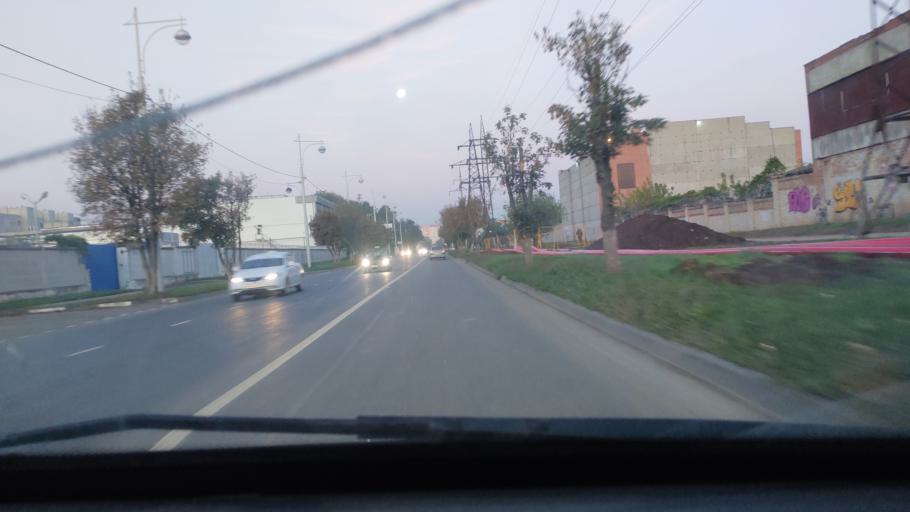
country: RU
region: Krasnodarskiy
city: Krasnodar
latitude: 45.0724
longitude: 38.9981
